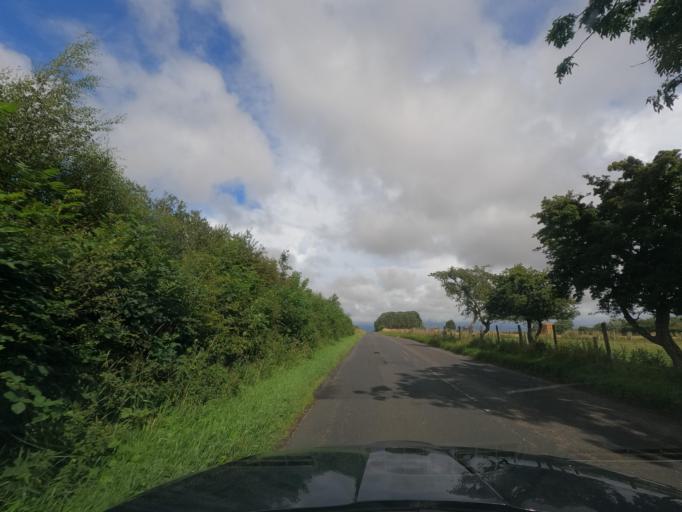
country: GB
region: England
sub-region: Northumberland
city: Lowick
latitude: 55.6399
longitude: -1.9929
